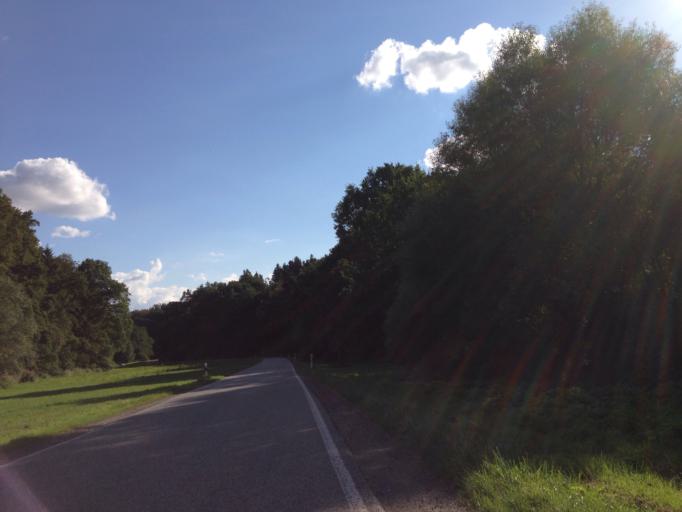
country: DE
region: Hesse
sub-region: Regierungsbezirk Giessen
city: Runkel
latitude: 50.4341
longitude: 8.1698
